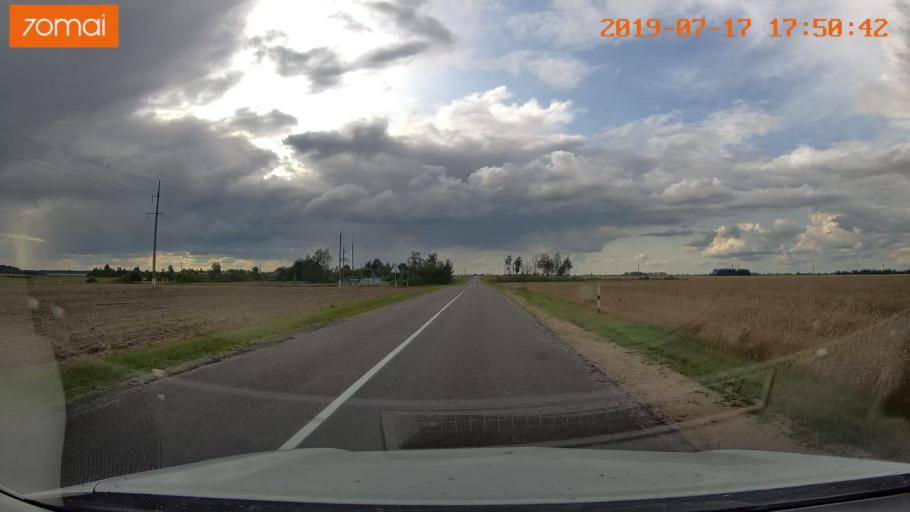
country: BY
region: Mogilev
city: Hlusha
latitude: 53.1443
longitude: 28.7984
